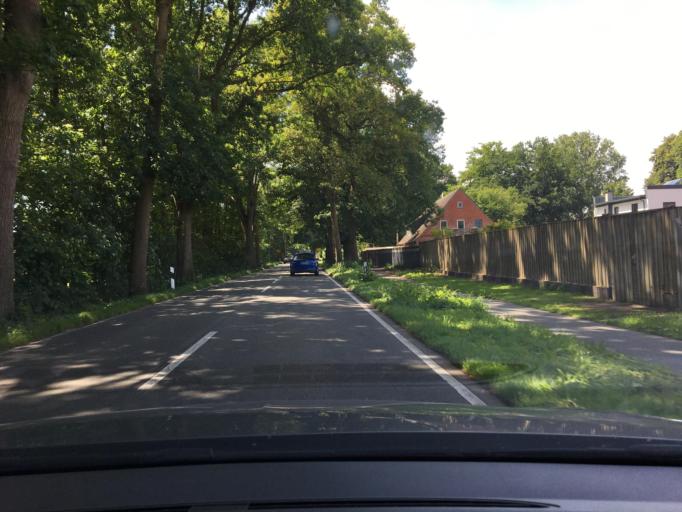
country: DE
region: Lower Saxony
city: Osterholz-Scharmbeck
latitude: 53.2507
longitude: 8.8239
